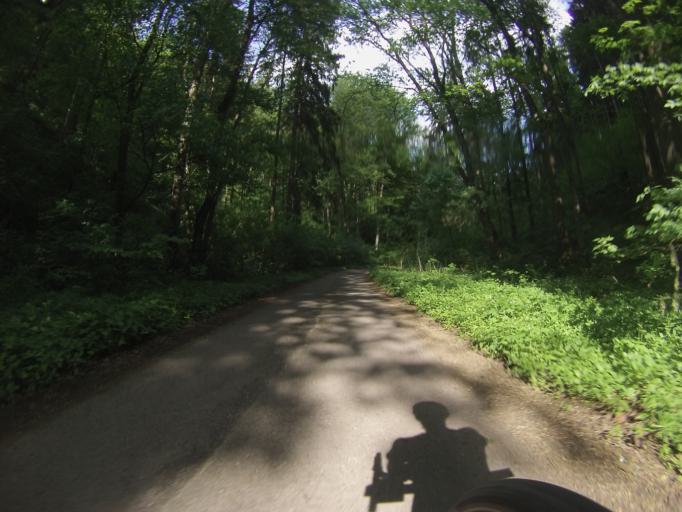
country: CZ
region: South Moravian
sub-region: Okres Blansko
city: Jedovnice
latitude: 49.3603
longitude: 16.7113
